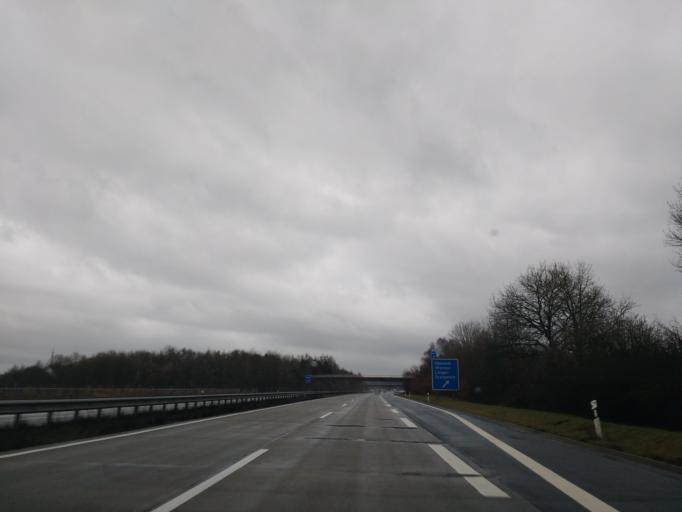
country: DE
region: Lower Saxony
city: Langen
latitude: 53.6268
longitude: 8.6652
